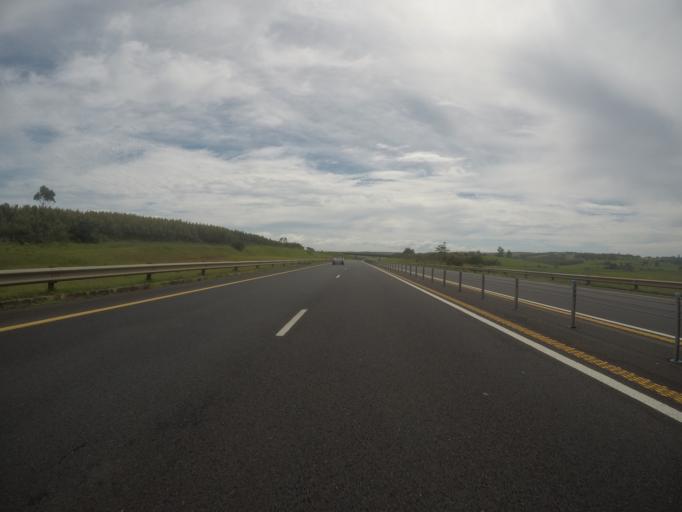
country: ZA
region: KwaZulu-Natal
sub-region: iLembe District Municipality
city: Mandeni
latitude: -29.0607
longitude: 31.6268
